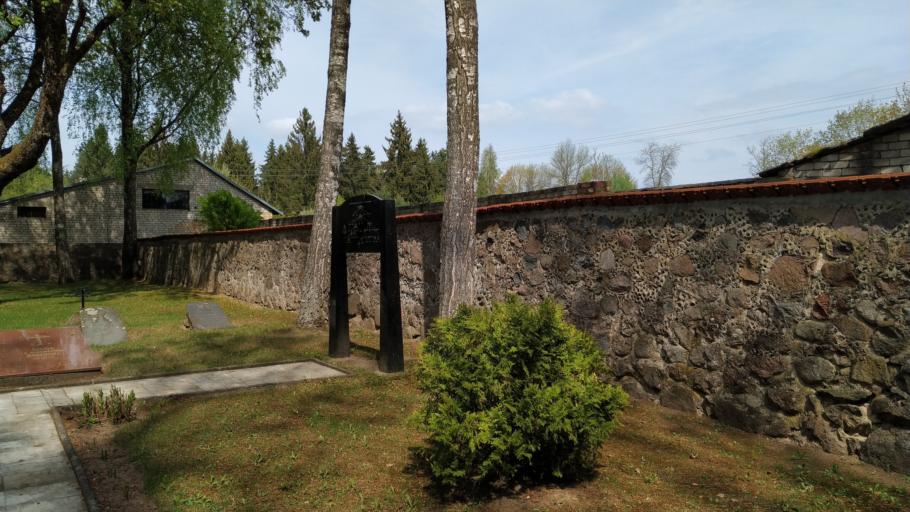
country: LT
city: Salcininkai
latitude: 54.4380
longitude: 25.2998
